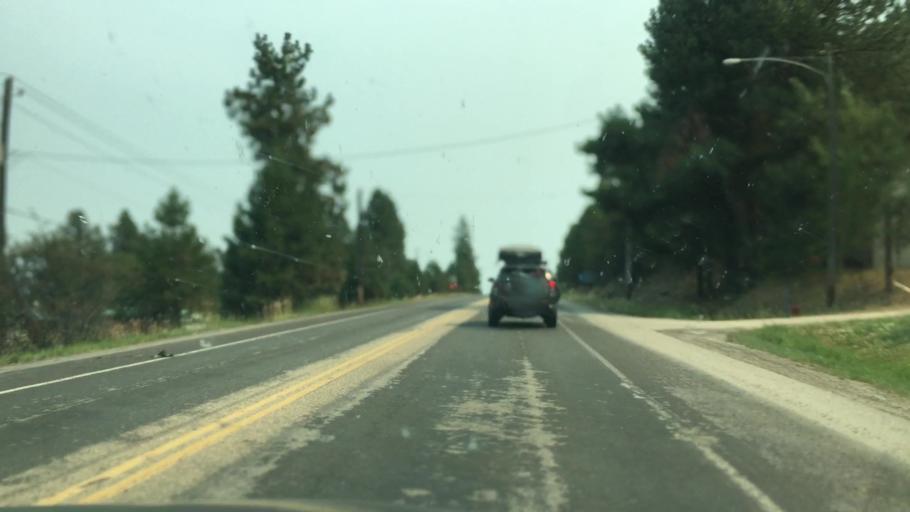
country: US
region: Idaho
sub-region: Valley County
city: Cascade
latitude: 44.5109
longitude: -116.0368
